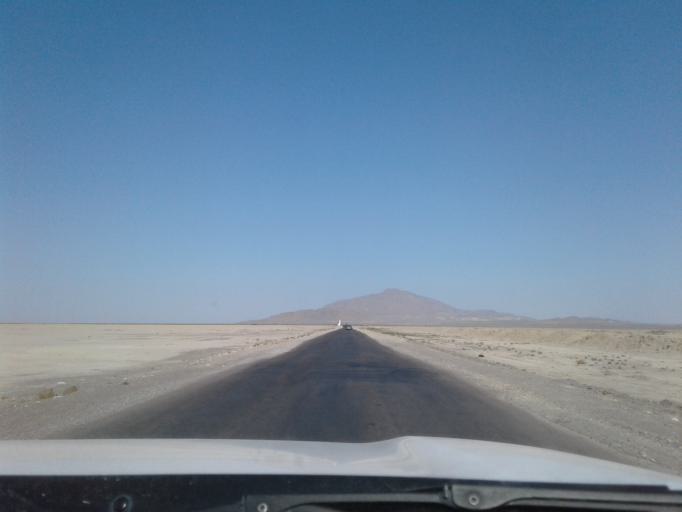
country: TM
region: Balkan
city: Gumdag
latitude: 39.2380
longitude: 54.7017
